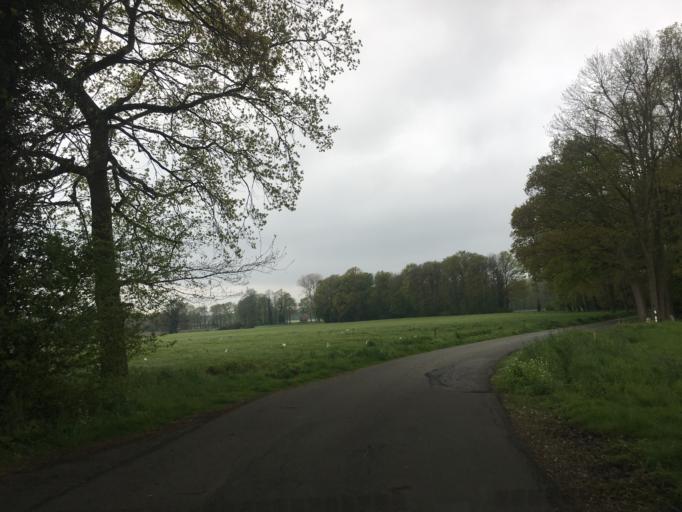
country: DE
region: North Rhine-Westphalia
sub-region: Regierungsbezirk Munster
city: Steinfurt
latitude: 52.1438
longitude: 7.3134
